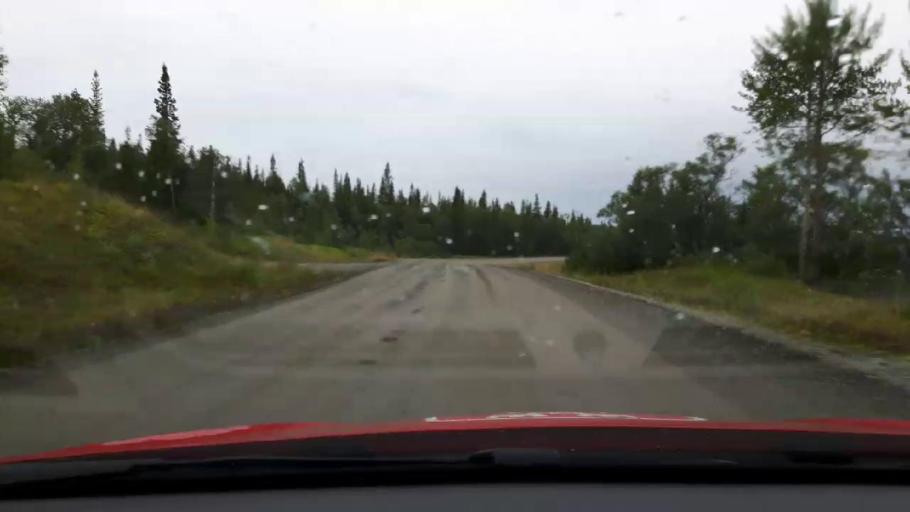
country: NO
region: Nord-Trondelag
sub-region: Meraker
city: Meraker
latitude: 63.5560
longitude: 12.3702
